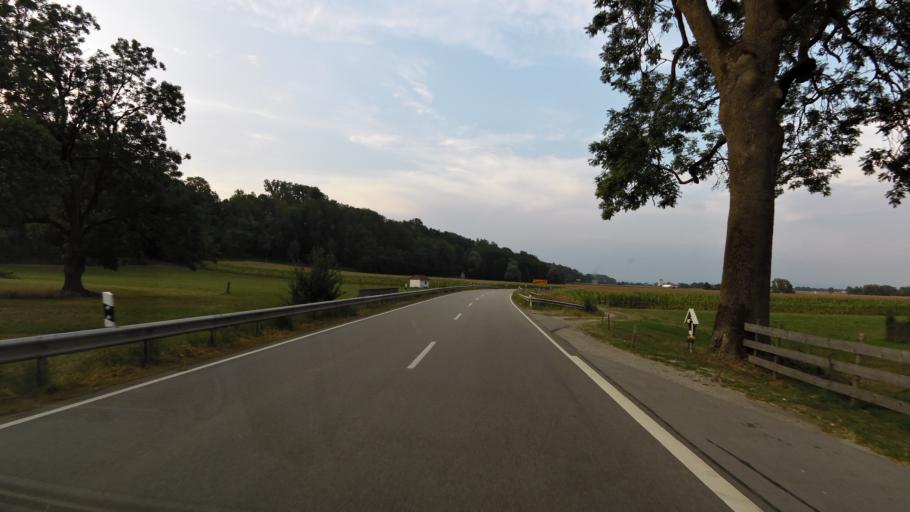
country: DE
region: Bavaria
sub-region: Lower Bavaria
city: Rotthalmunster
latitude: 48.3352
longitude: 13.2280
